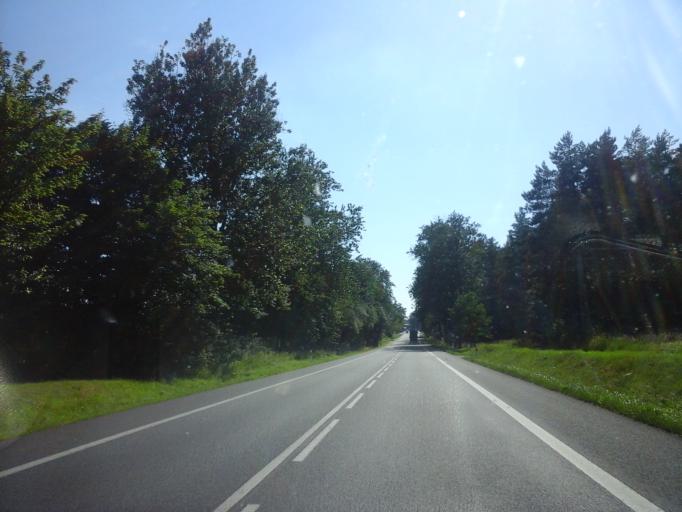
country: PL
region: West Pomeranian Voivodeship
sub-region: Powiat kolobrzeski
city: Ryman
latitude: 53.9498
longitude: 15.5428
